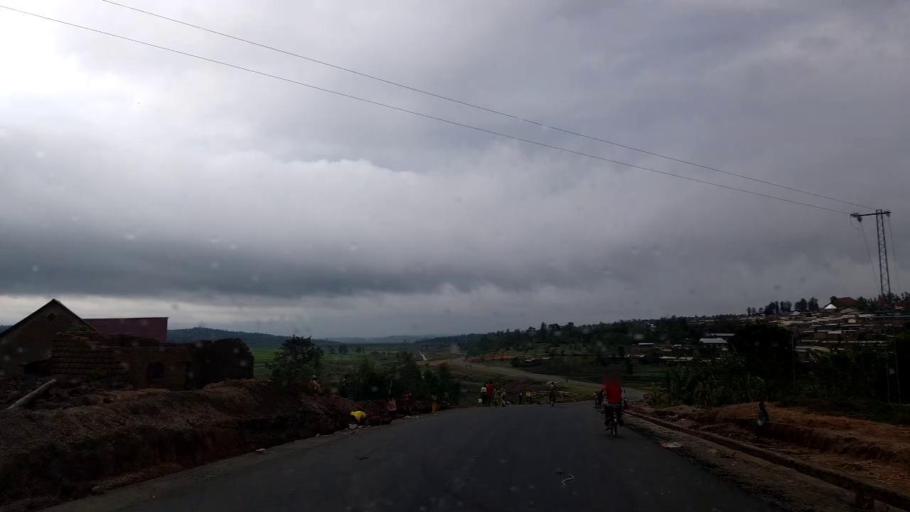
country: RW
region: Northern Province
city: Byumba
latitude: -1.4483
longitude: 30.2470
